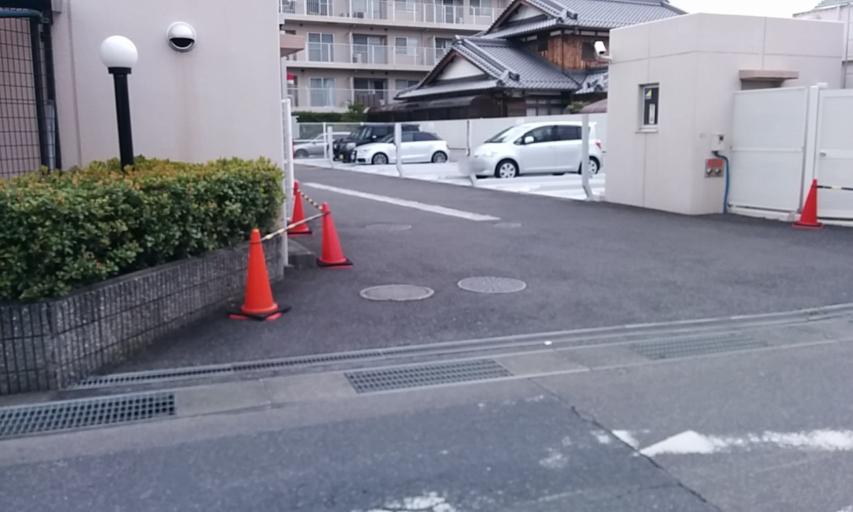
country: JP
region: Shiga Prefecture
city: Kusatsu
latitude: 35.0120
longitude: 135.9567
